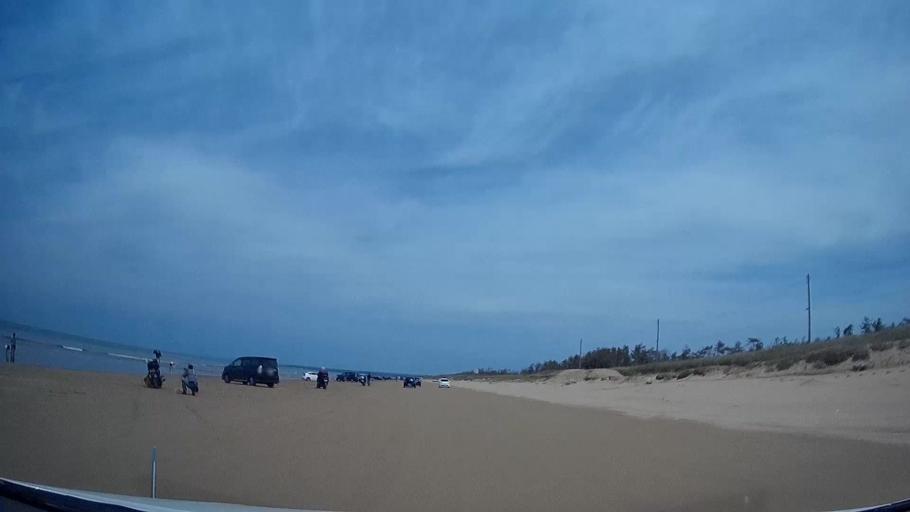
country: JP
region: Ishikawa
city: Hakui
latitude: 36.8424
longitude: 136.7504
